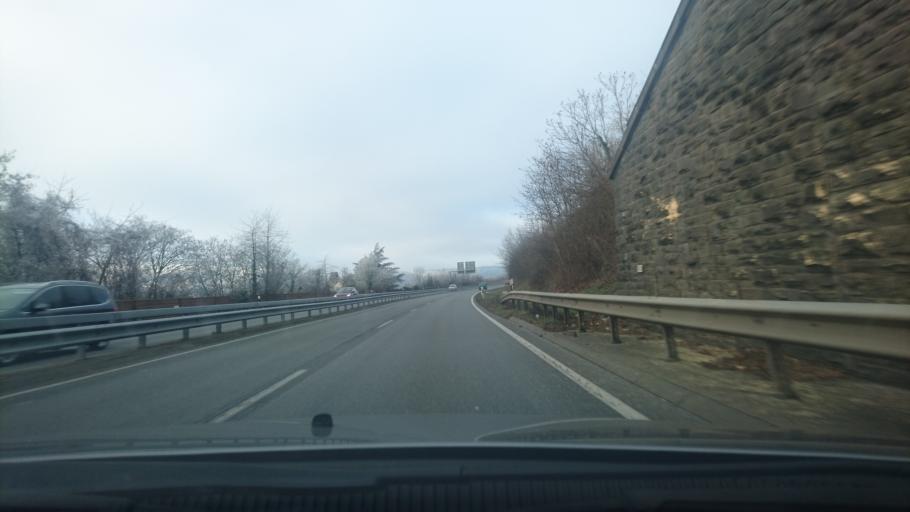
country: DE
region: Rheinland-Pfalz
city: Lahnstein
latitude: 50.3141
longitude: 7.6044
